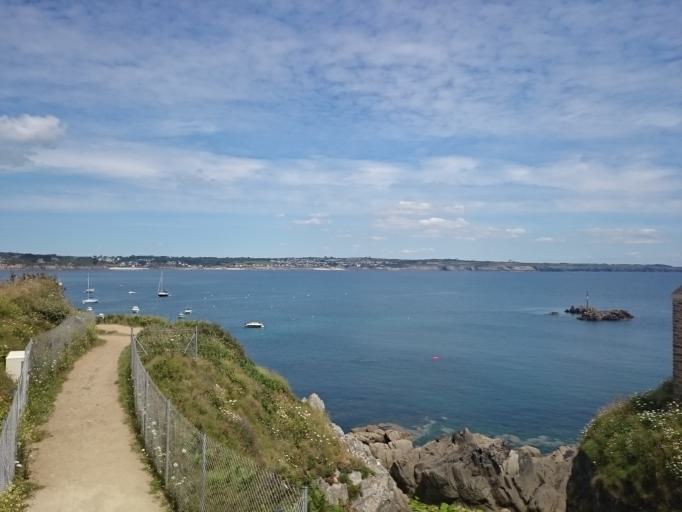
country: FR
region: Brittany
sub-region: Departement du Finistere
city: Plougonvelin
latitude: 48.3378
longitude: -4.6987
